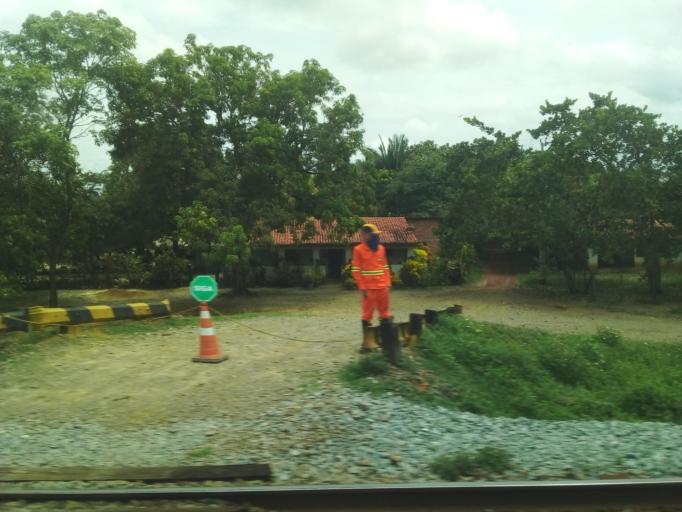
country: BR
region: Maranhao
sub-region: Arari
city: Arari
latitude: -3.5684
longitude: -44.7794
